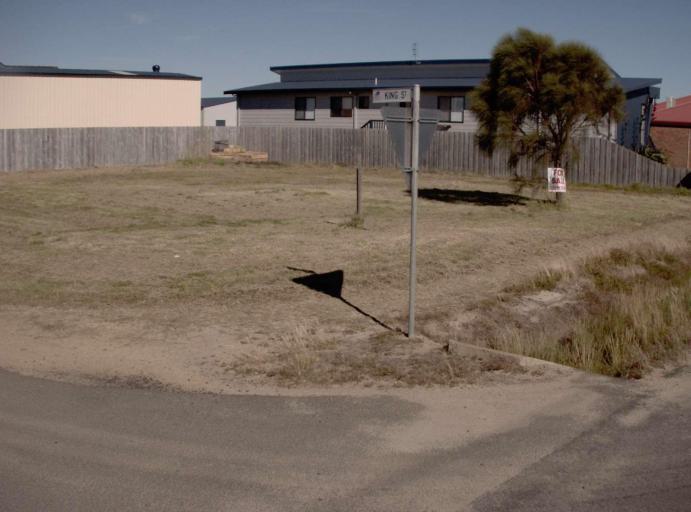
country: AU
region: Victoria
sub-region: Latrobe
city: Traralgon
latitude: -38.6678
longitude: 146.6901
